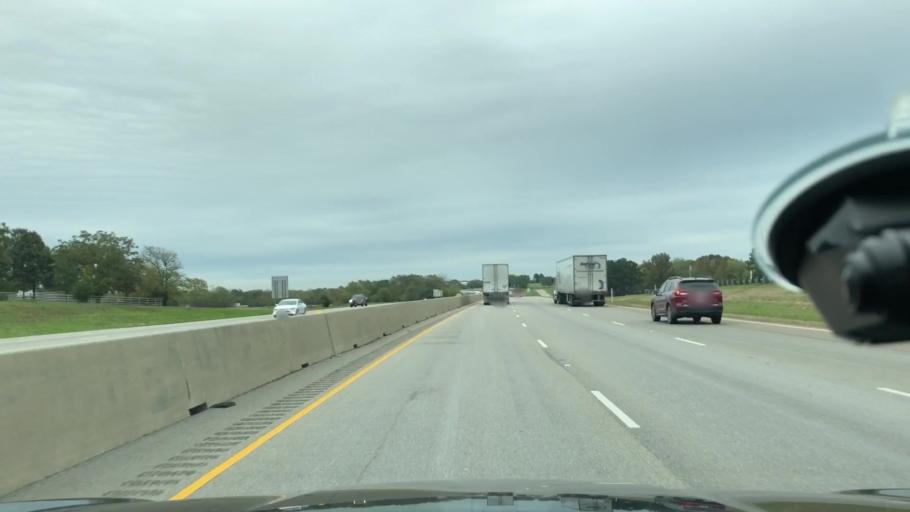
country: US
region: Texas
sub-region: Franklin County
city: Mount Vernon
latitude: 33.1620
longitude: -95.2124
